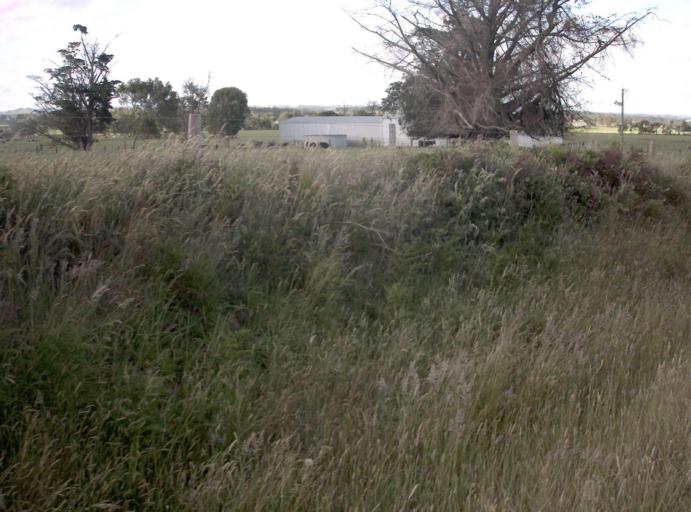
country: AU
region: Victoria
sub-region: Bass Coast
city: North Wonthaggi
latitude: -38.5348
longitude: 145.8717
